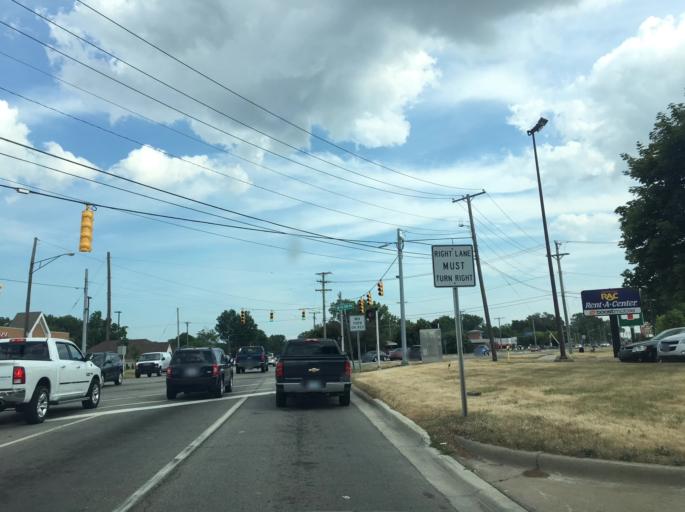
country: US
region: Michigan
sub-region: Macomb County
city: Utica
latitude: 42.6114
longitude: -83.0321
